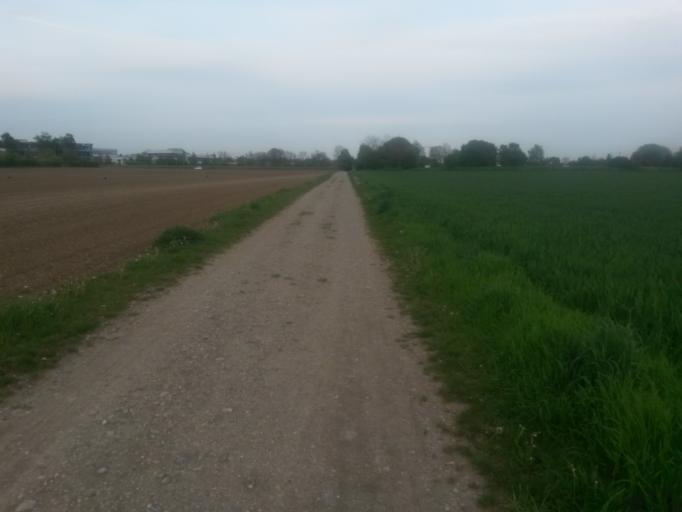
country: DE
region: Bavaria
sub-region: Upper Bavaria
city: Unterhaching
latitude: 48.0590
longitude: 11.6084
